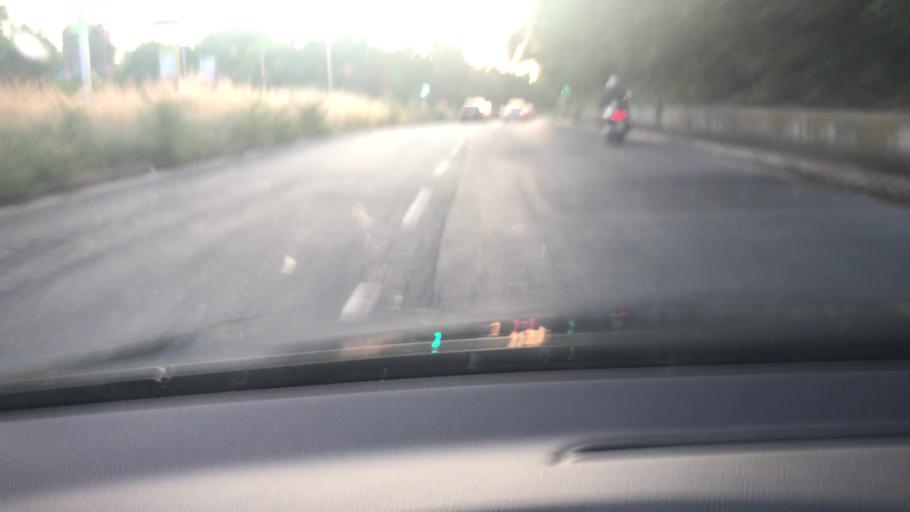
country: IT
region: Latium
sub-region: Citta metropolitana di Roma Capitale
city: Rome
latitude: 41.9320
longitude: 12.5598
